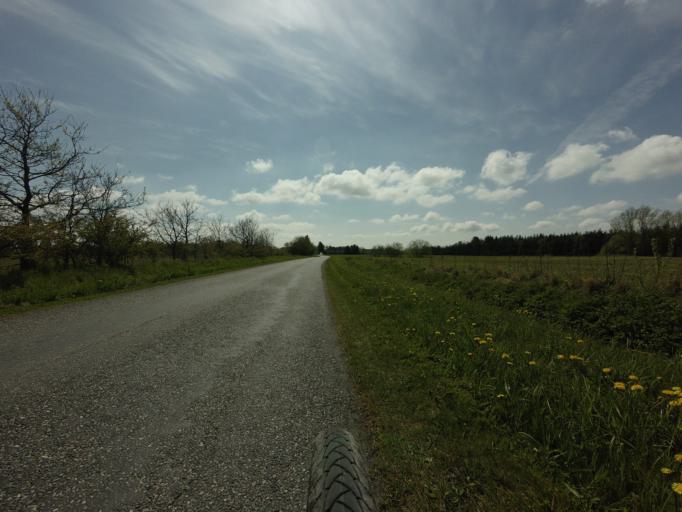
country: DK
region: North Denmark
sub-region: Jammerbugt Kommune
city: Brovst
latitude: 57.1495
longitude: 9.5538
